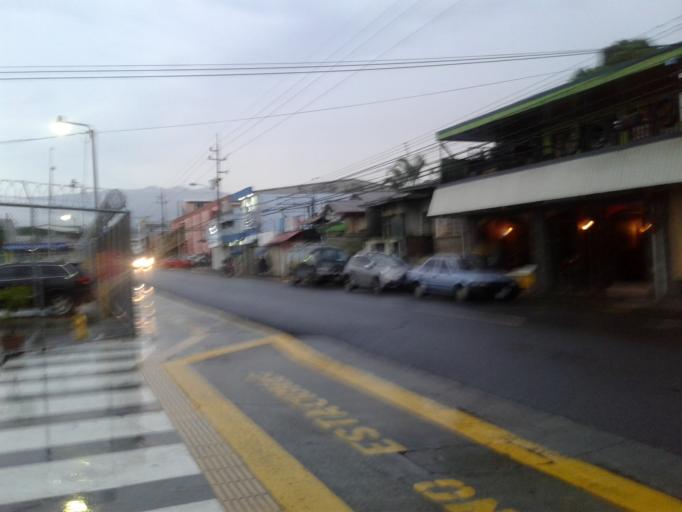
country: CR
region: Heredia
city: Heredia
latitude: 9.9994
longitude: -84.1219
